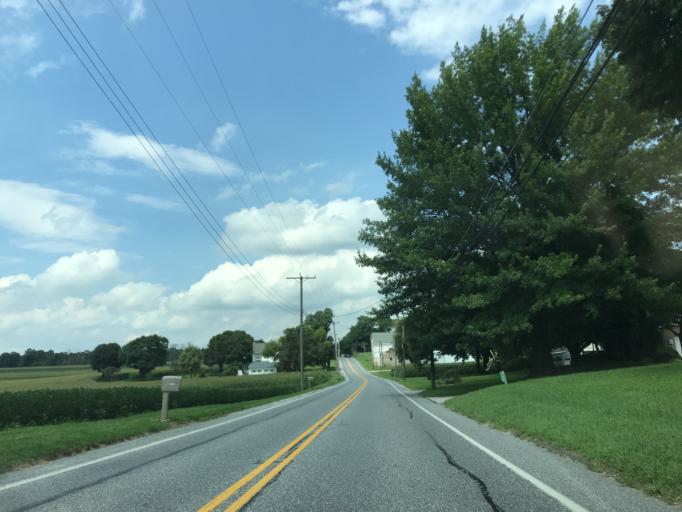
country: US
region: Pennsylvania
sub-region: York County
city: Red Lion
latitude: 39.8492
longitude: -76.6204
